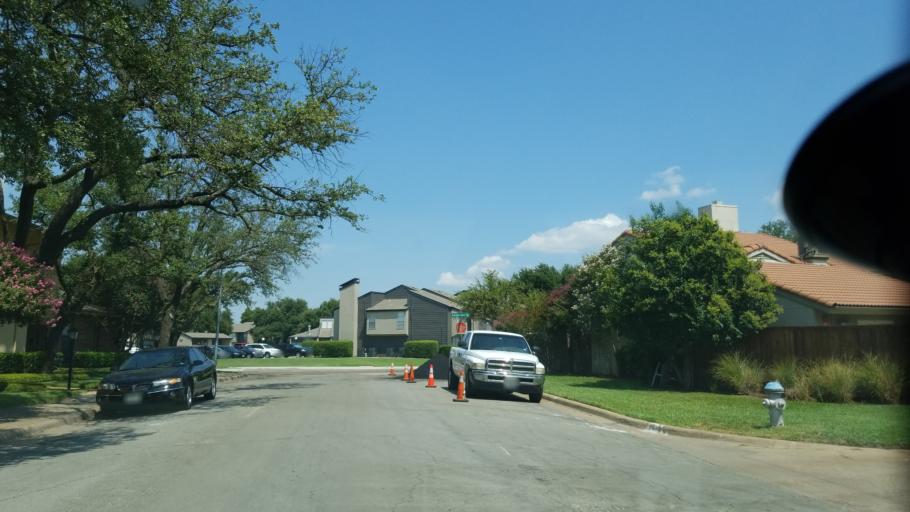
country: US
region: Texas
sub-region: Dallas County
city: Richardson
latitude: 32.9171
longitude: -96.7388
